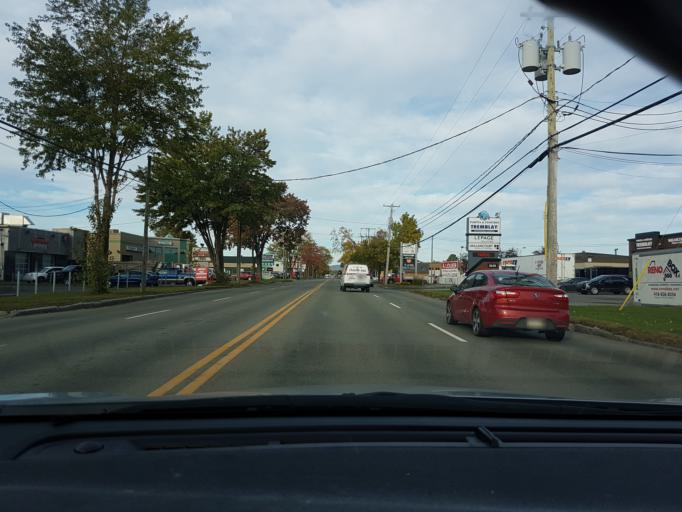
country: CA
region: Quebec
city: L'Ancienne-Lorette
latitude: 46.8065
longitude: -71.2992
